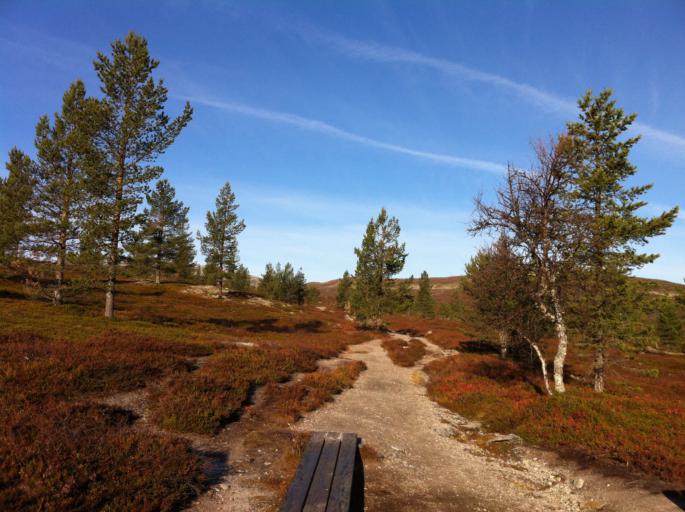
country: NO
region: Hedmark
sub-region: Engerdal
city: Engerdal
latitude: 62.1079
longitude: 12.2839
